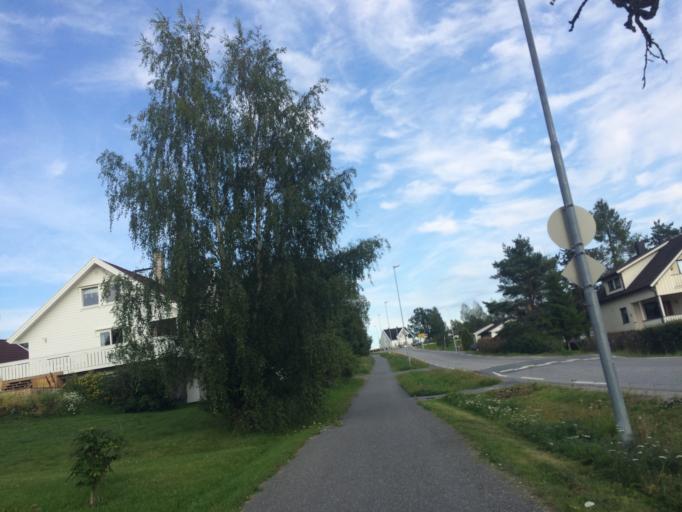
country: NO
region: Akershus
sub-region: Ski
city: Ski
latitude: 59.6822
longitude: 10.8807
